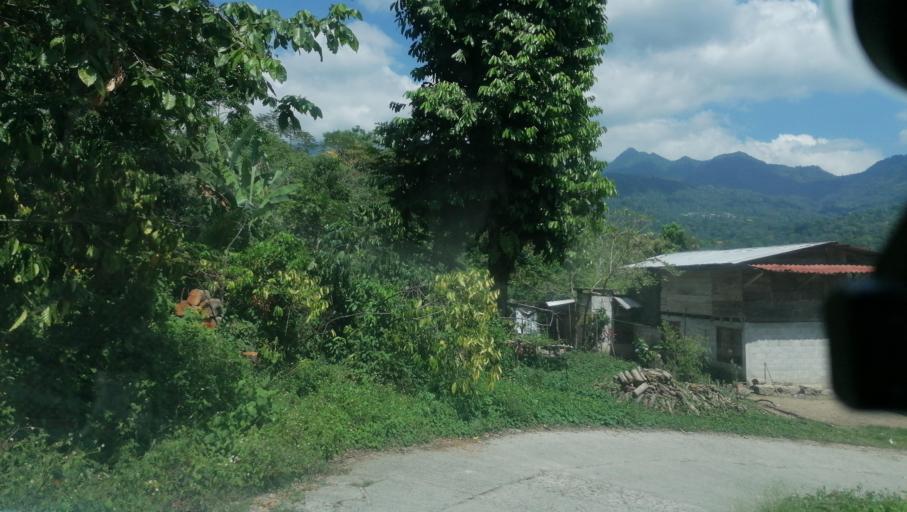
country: MX
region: Chiapas
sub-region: Union Juarez
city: Santo Domingo
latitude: 15.0371
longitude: -92.1431
